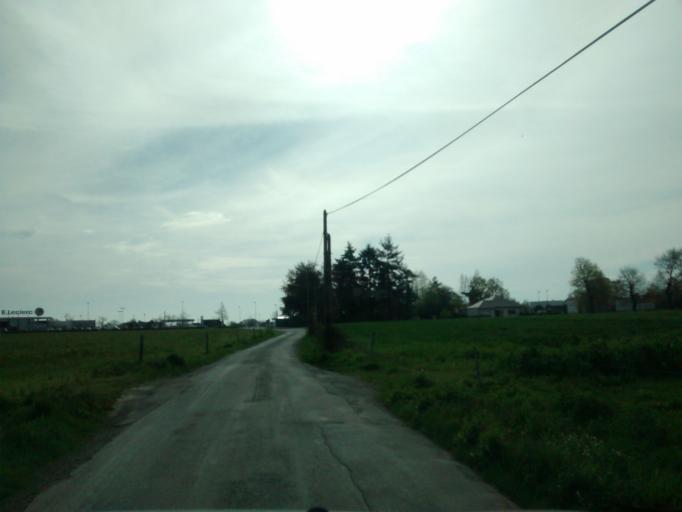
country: FR
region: Brittany
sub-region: Departement d'Ille-et-Vilaine
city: Acigne
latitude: 48.1212
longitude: -1.5346
